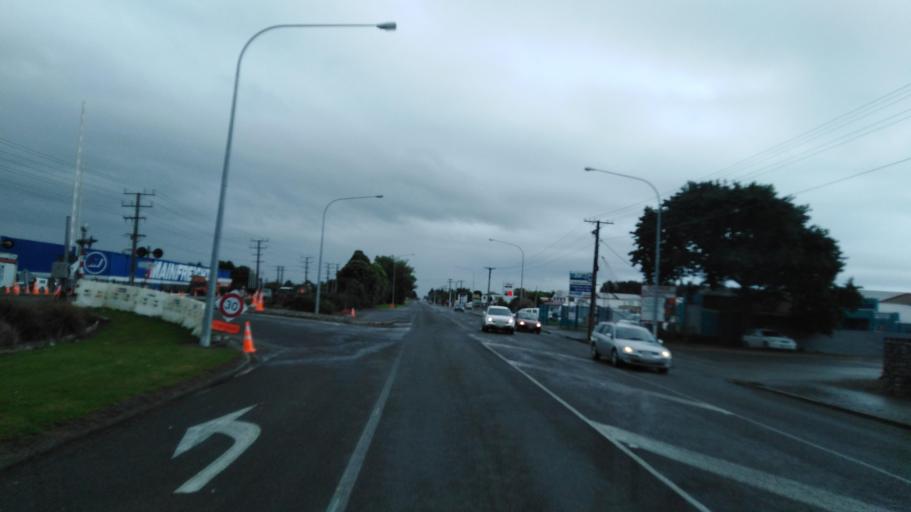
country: NZ
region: Manawatu-Wanganui
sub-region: Horowhenua District
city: Levin
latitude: -40.6358
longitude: 175.2731
